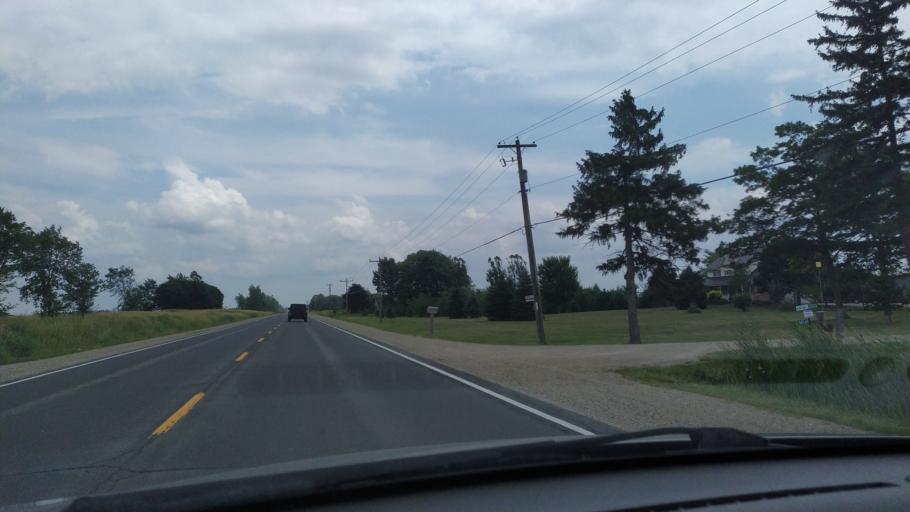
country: CA
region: Ontario
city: Stratford
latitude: 43.3700
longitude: -80.8825
